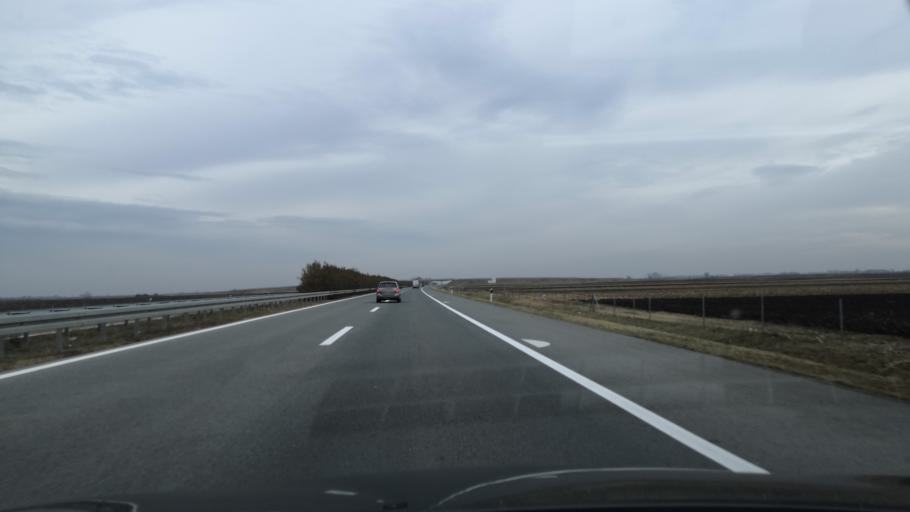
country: RS
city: Kisac
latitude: 45.3547
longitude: 19.7569
